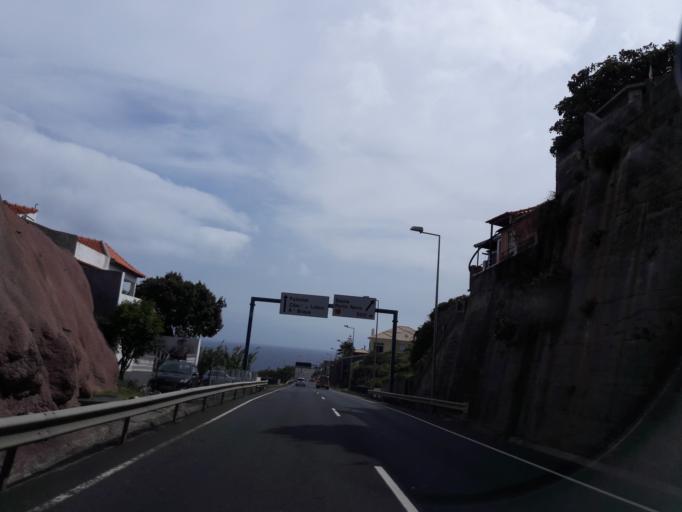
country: PT
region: Madeira
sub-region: Santa Cruz
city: Santa Cruz
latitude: 32.6734
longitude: -16.8040
